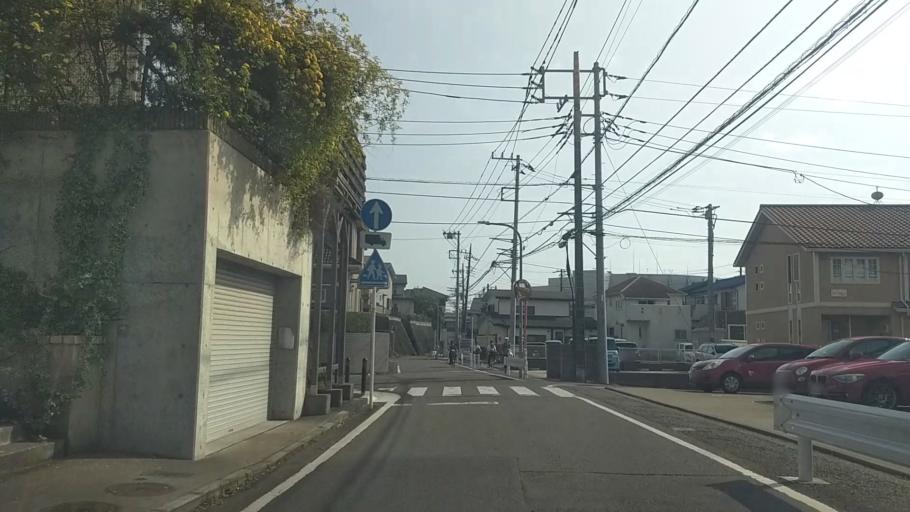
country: JP
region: Kanagawa
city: Kamakura
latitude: 35.3705
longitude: 139.5551
